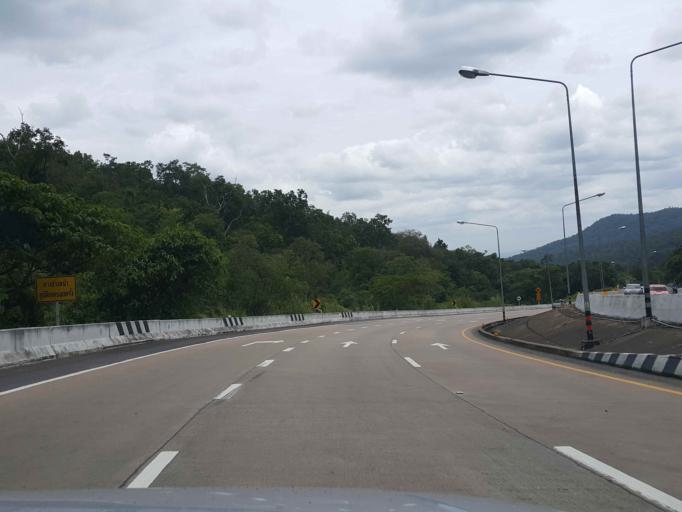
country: TH
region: Lamphun
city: Mae Tha
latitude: 18.4244
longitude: 99.2094
